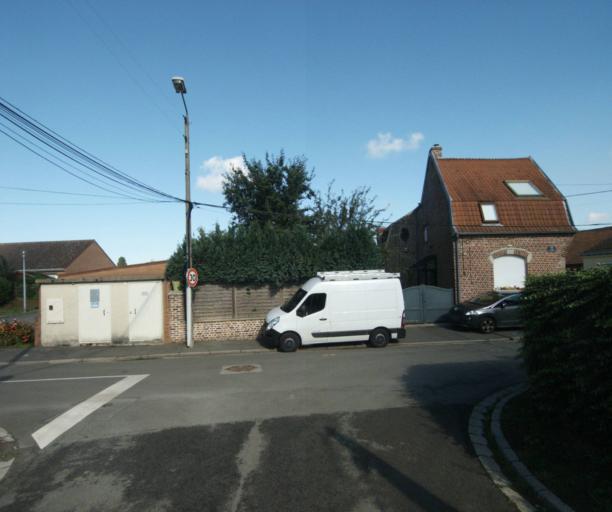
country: FR
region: Nord-Pas-de-Calais
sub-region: Departement du Nord
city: Toufflers
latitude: 50.6575
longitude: 3.2343
